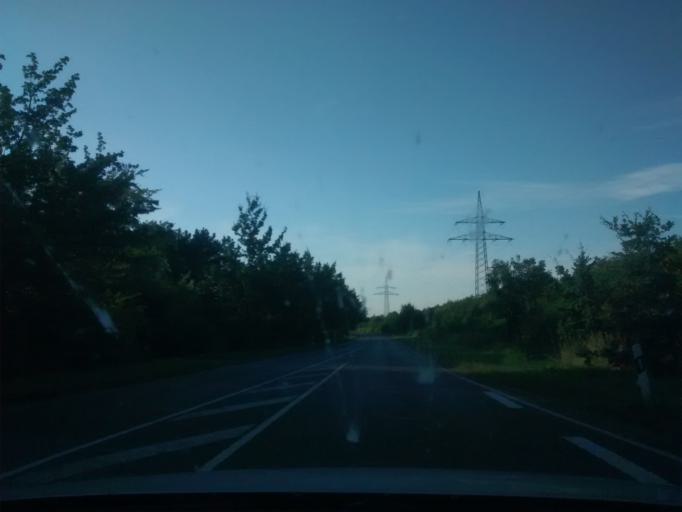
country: DE
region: Hesse
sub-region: Regierungsbezirk Kassel
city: Lohfelden
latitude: 51.2651
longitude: 9.5102
